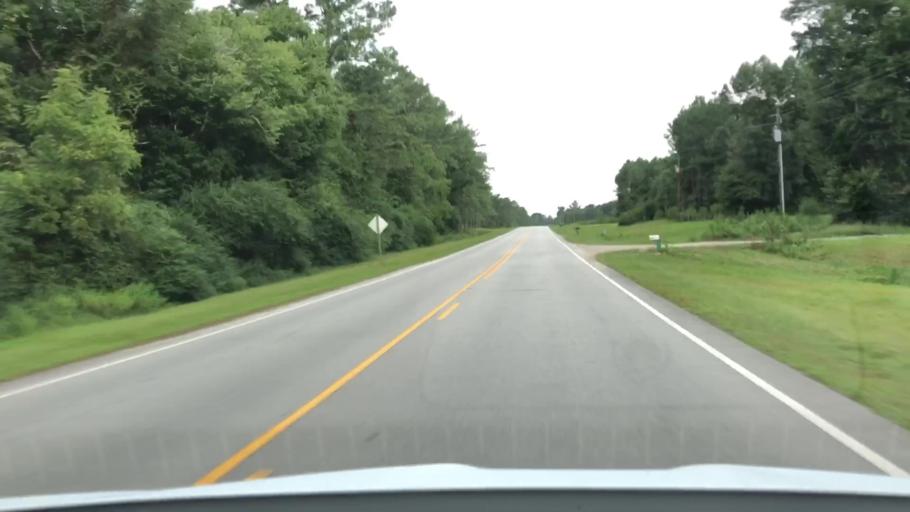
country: US
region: North Carolina
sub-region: Jones County
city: Trenton
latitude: 35.0125
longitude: -77.2914
